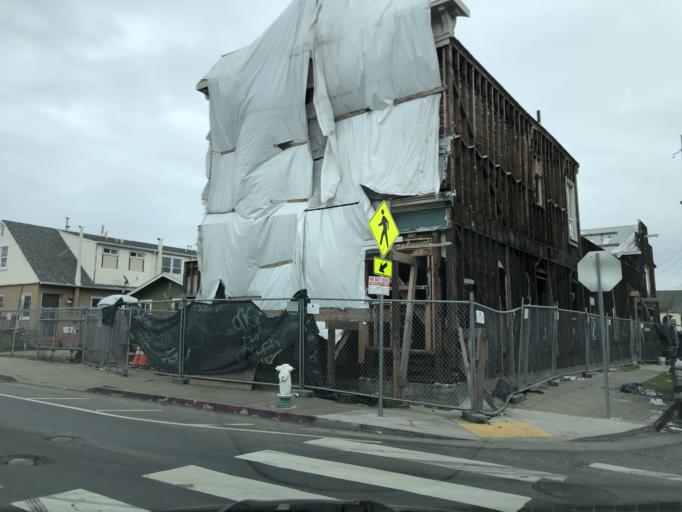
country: US
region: California
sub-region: Alameda County
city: San Leandro
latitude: 37.7424
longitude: -122.1748
